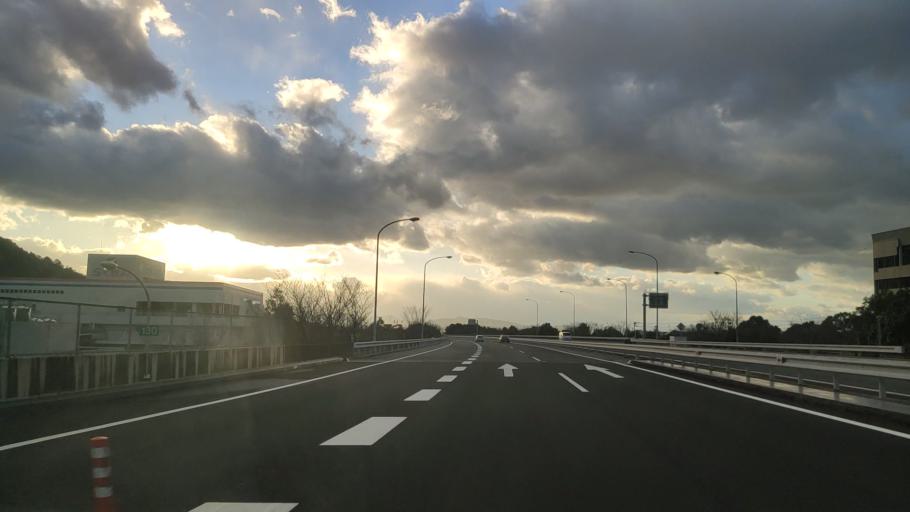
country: JP
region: Ehime
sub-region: Shikoku-chuo Shi
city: Matsuyama
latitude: 33.7943
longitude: 132.9032
